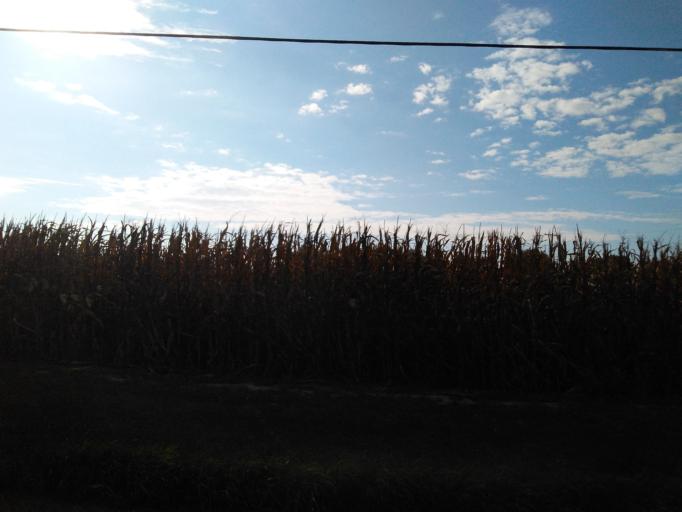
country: US
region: Illinois
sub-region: Bond County
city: Greenville
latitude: 38.8761
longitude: -89.4143
